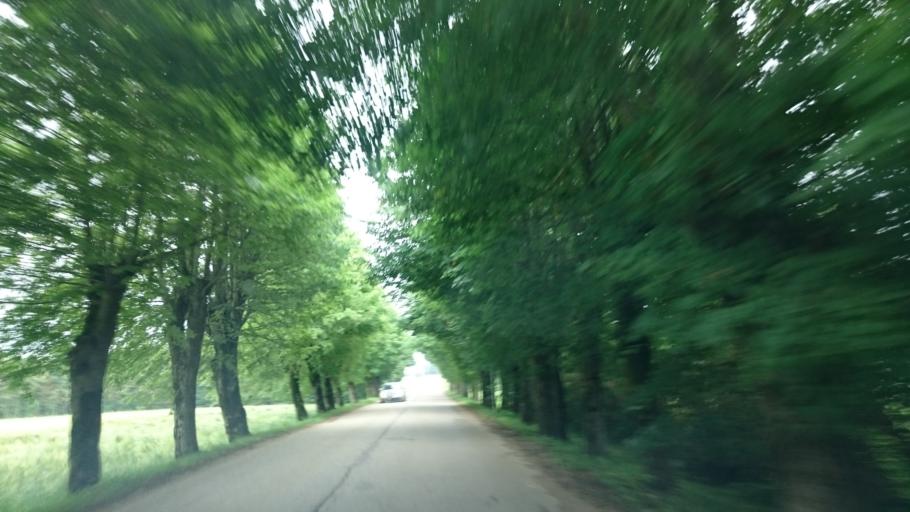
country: LV
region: Durbe
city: Liegi
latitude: 56.7303
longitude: 21.4010
